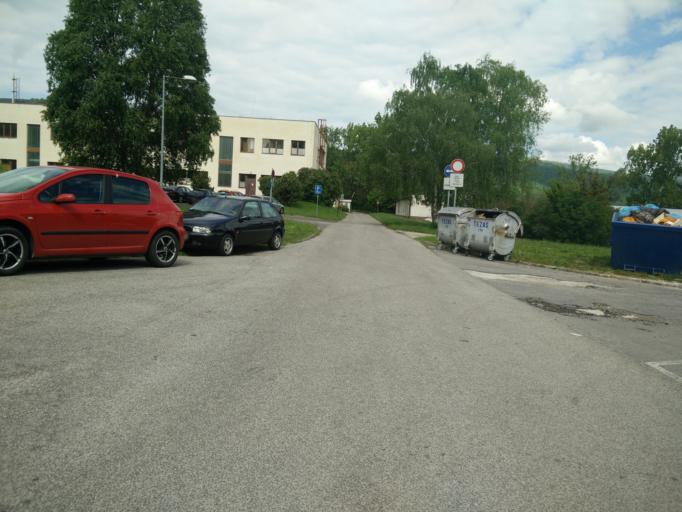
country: SK
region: Nitriansky
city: Bojnice
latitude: 48.7867
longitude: 18.5895
